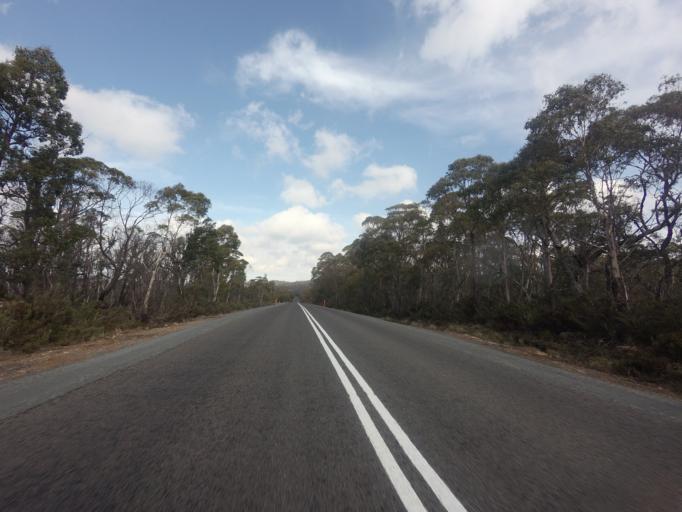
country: AU
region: Tasmania
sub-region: Meander Valley
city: Deloraine
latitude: -41.8321
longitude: 146.6777
